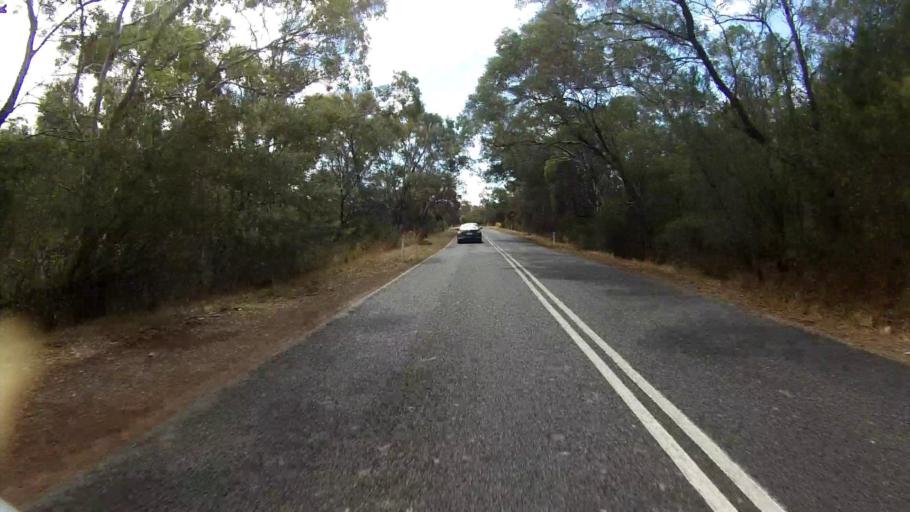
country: AU
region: Tasmania
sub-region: Sorell
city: Sorell
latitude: -42.1516
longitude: 148.0684
